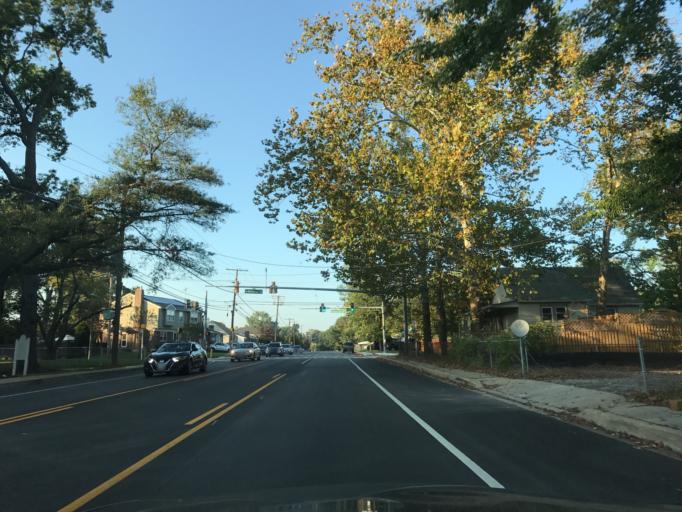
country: US
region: Maryland
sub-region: Anne Arundel County
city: South Gate
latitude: 39.1439
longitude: -76.6186
